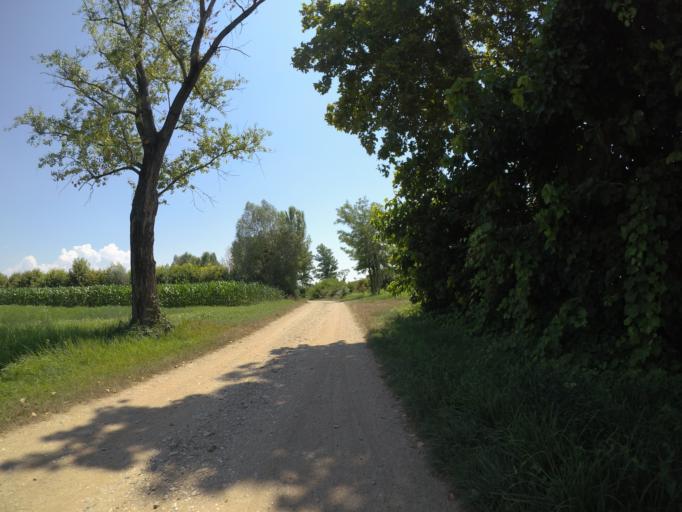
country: IT
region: Friuli Venezia Giulia
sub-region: Provincia di Udine
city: Mortegliano
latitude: 45.9401
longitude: 13.1788
